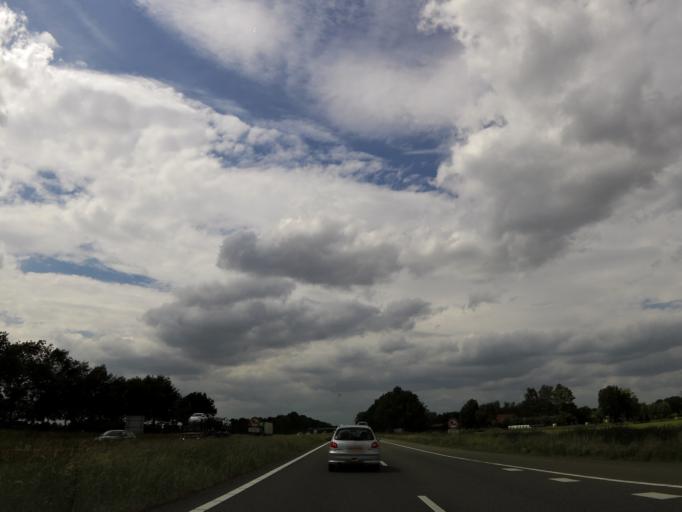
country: NL
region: Limburg
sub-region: Gemeente Nederweert
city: Nederweert
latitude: 51.2569
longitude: 5.7611
